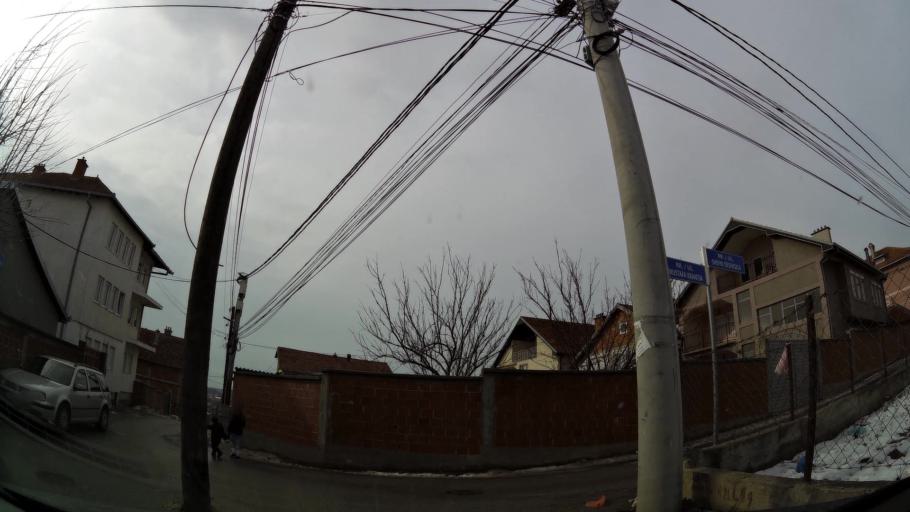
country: XK
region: Pristina
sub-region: Komuna e Prishtines
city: Pristina
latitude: 42.6830
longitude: 21.1678
